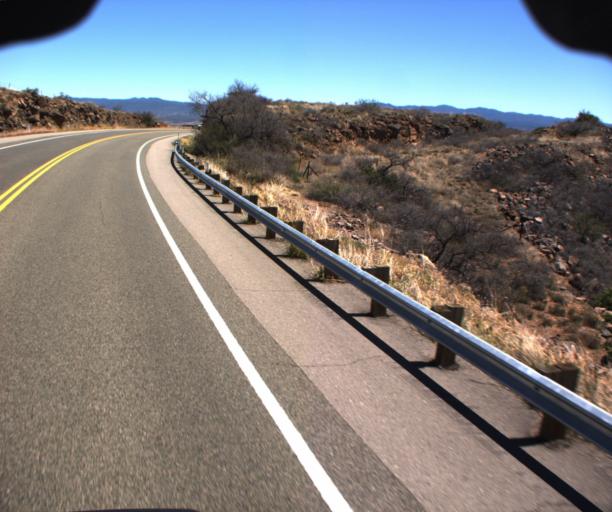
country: US
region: Arizona
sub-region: Yavapai County
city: Congress
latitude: 34.3270
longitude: -112.6967
